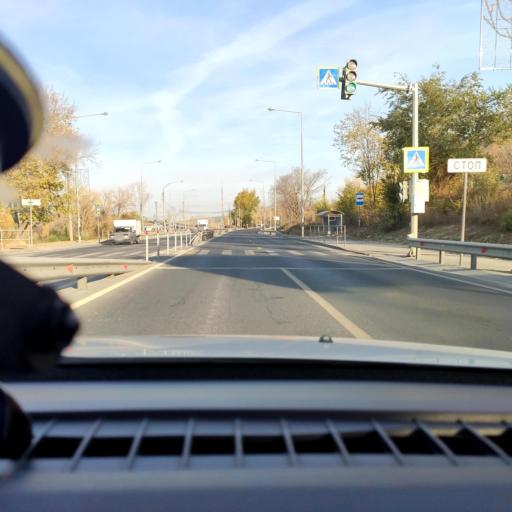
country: RU
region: Samara
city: Volzhskiy
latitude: 53.4069
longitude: 50.1439
